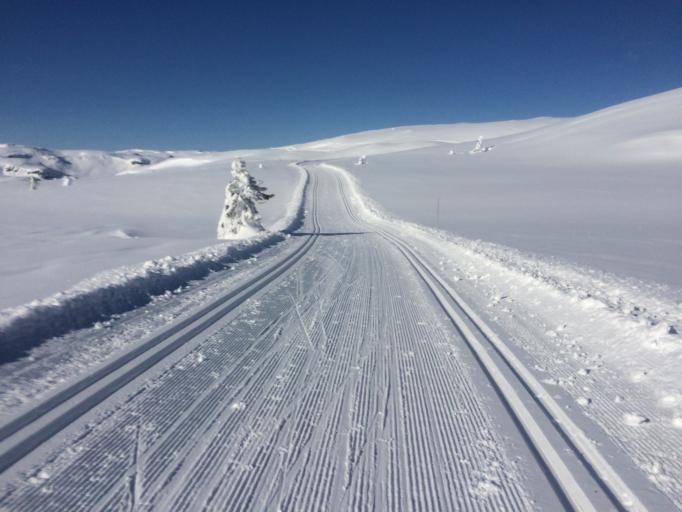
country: NO
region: Oppland
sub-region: Ringebu
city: Ringebu
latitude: 61.3672
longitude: 10.0751
